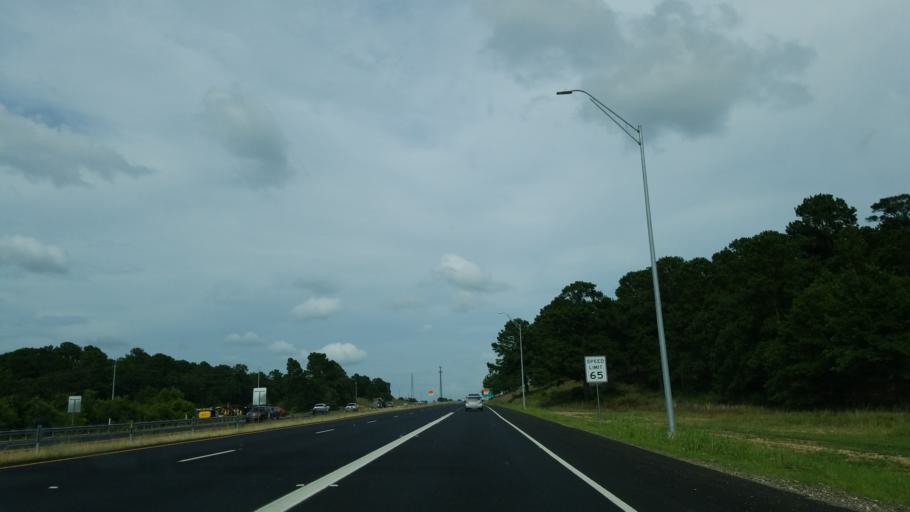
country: US
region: Texas
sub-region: Bastrop County
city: Bastrop
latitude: 30.1049
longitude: -97.3019
